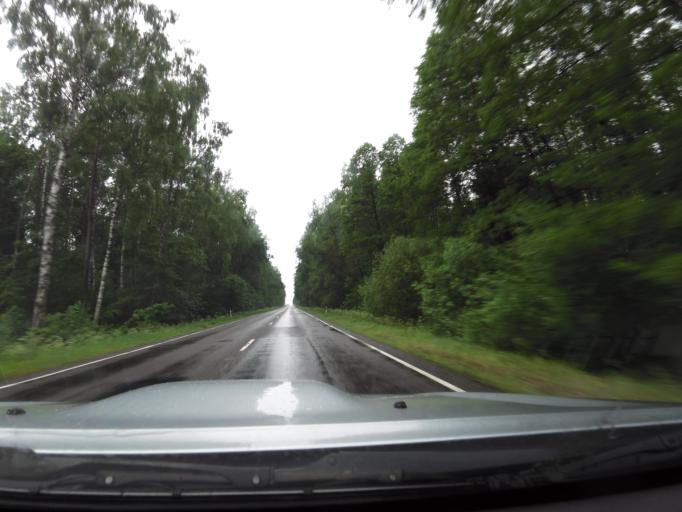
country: LT
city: Simnas
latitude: 54.5598
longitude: 23.6842
